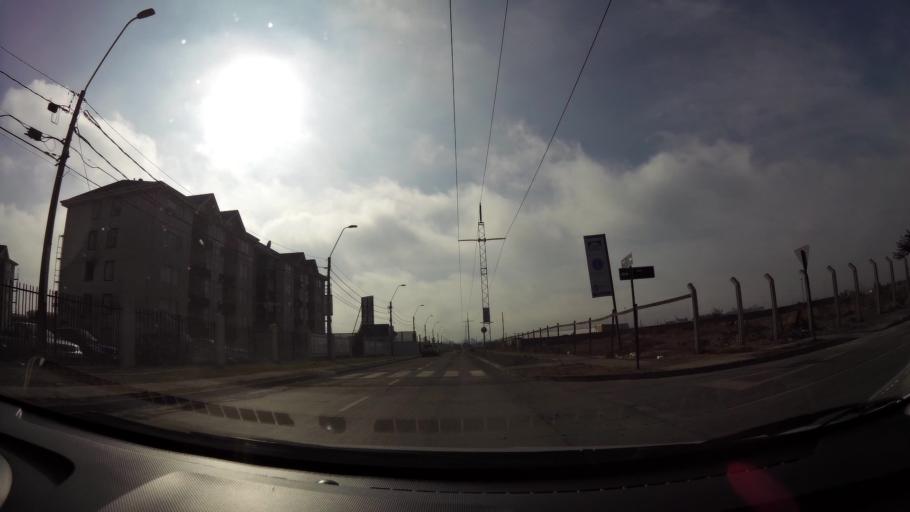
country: CL
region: Biobio
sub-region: Provincia de Concepcion
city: Concepcion
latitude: -36.7994
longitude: -73.1095
